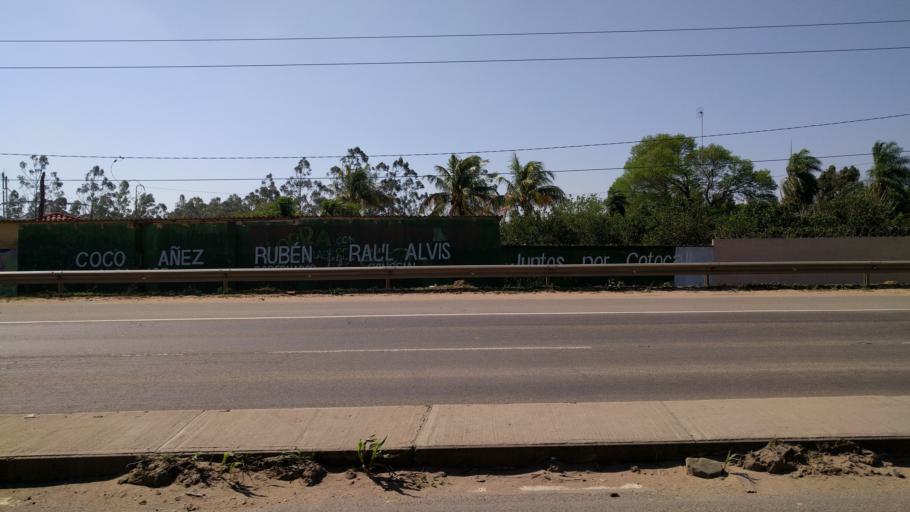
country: BO
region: Santa Cruz
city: Cotoca
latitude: -17.7642
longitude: -63.0636
